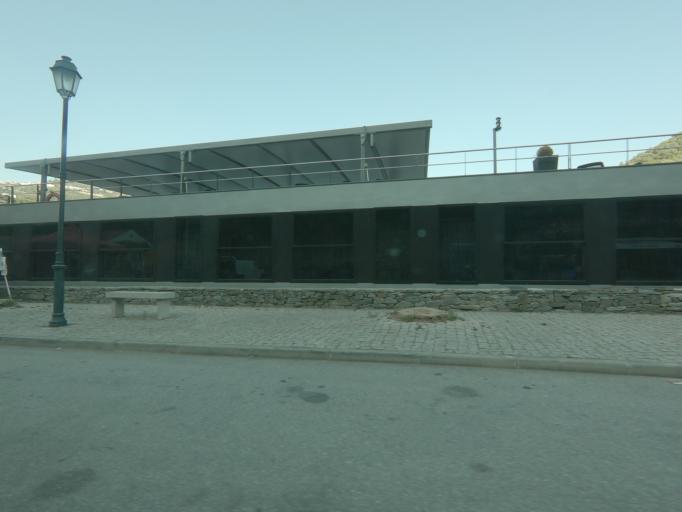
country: PT
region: Vila Real
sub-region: Sabrosa
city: Vilela
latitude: 41.1890
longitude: -7.5498
